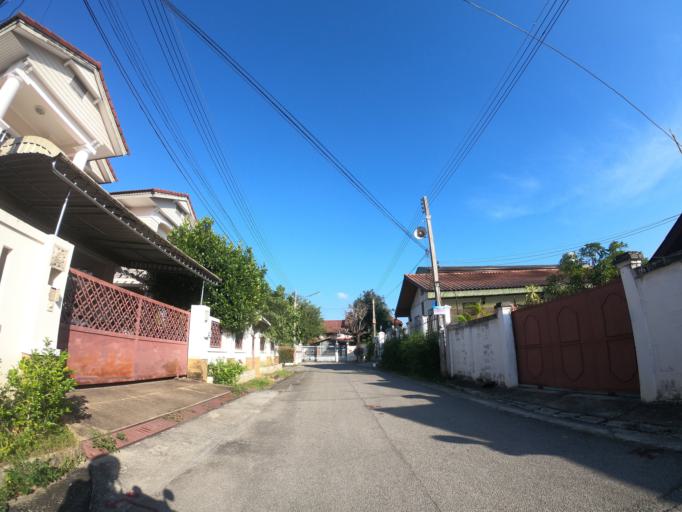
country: TH
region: Chiang Mai
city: Chiang Mai
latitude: 18.7545
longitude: 98.9710
